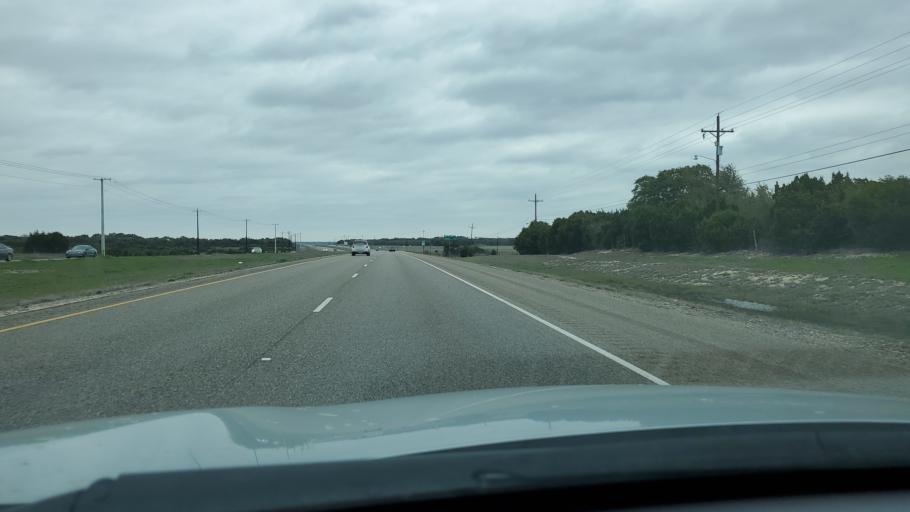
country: US
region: Texas
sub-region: Williamson County
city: Florence
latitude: 30.7975
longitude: -97.7677
